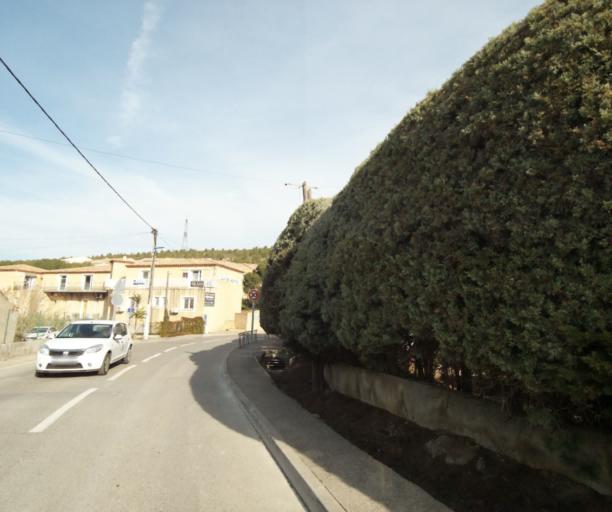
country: FR
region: Provence-Alpes-Cote d'Azur
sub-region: Departement des Bouches-du-Rhone
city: Ensues-la-Redonne
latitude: 43.3547
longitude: 5.1973
